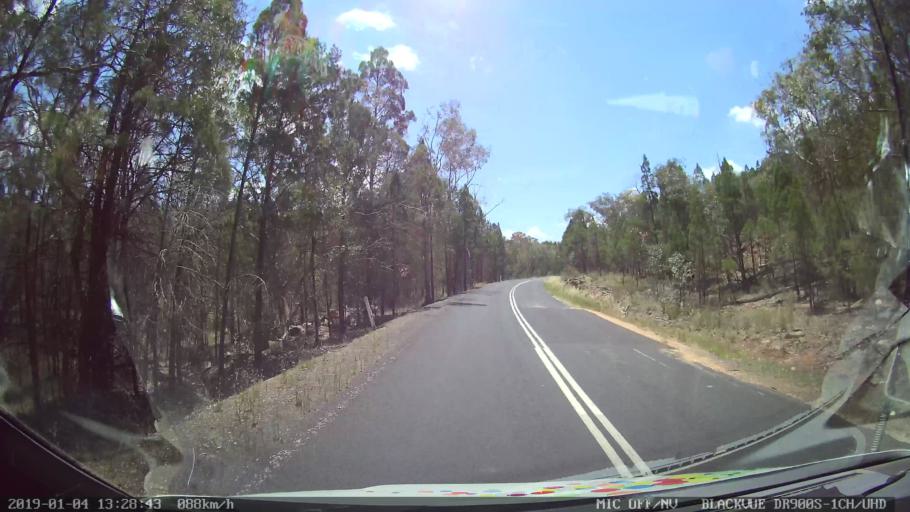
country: AU
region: New South Wales
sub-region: Parkes
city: Peak Hill
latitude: -32.6555
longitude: 148.5495
